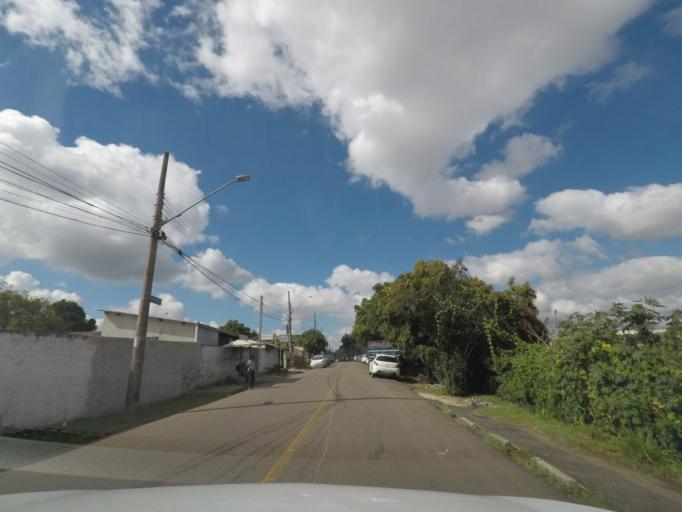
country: BR
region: Parana
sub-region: Sao Jose Dos Pinhais
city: Sao Jose dos Pinhais
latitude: -25.4832
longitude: -49.2366
